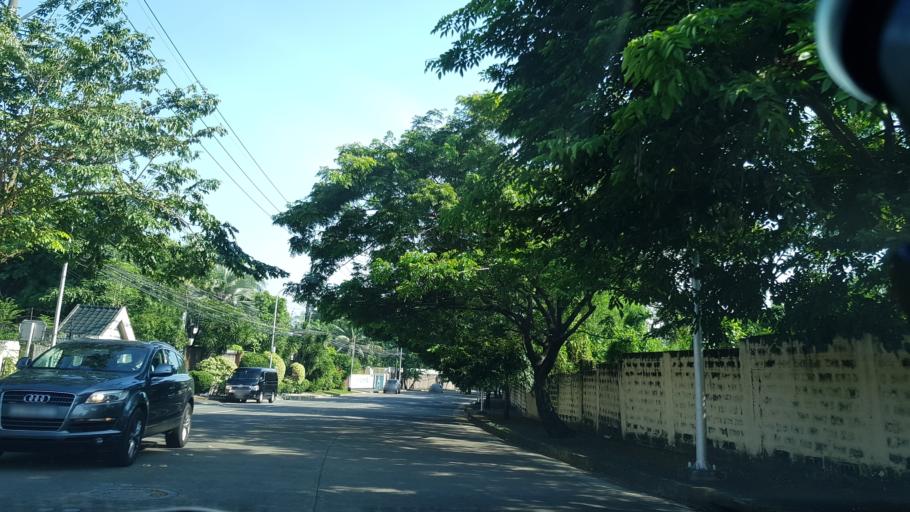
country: PH
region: Metro Manila
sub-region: Pasig
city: Pasig City
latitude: 14.5977
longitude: 121.0721
